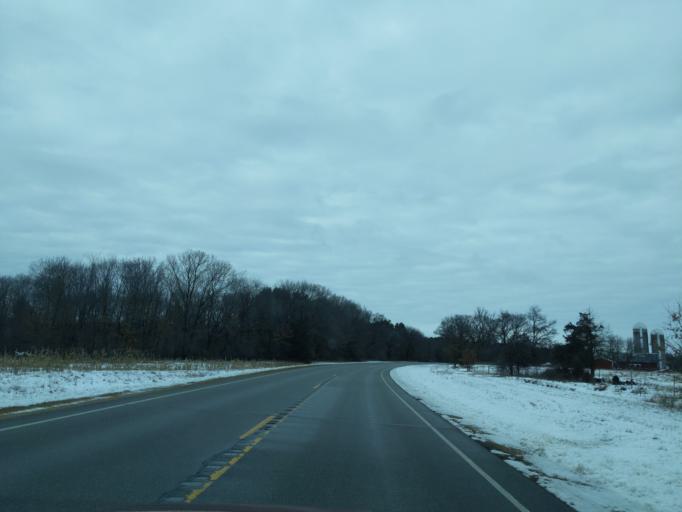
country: US
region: Wisconsin
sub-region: Waushara County
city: Wautoma
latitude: 43.9432
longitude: -89.3164
